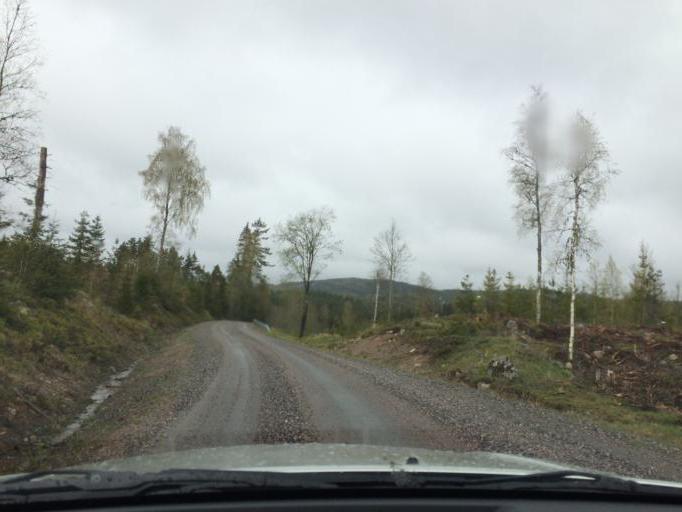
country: SE
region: Dalarna
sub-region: Ludvika Kommun
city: Abborrberget
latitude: 60.0199
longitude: 14.6047
